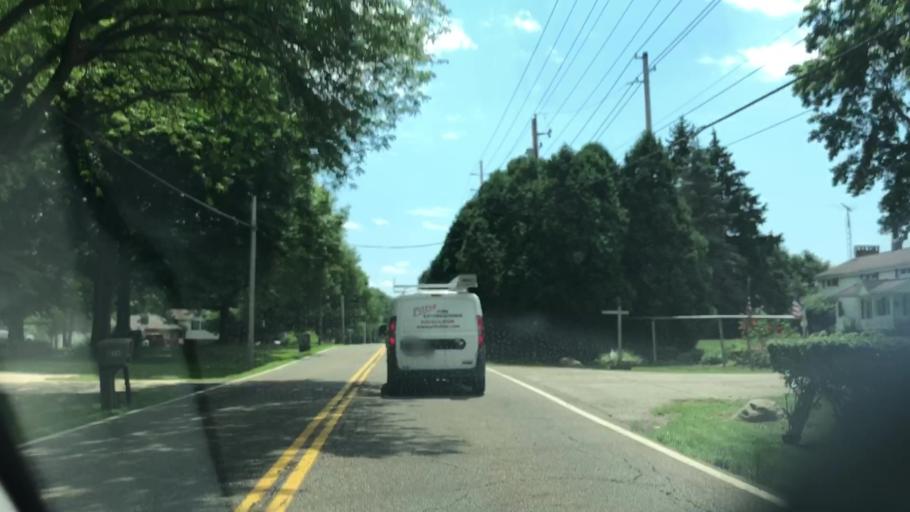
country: US
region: Ohio
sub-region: Summit County
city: Greensburg
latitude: 40.9004
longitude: -81.4982
